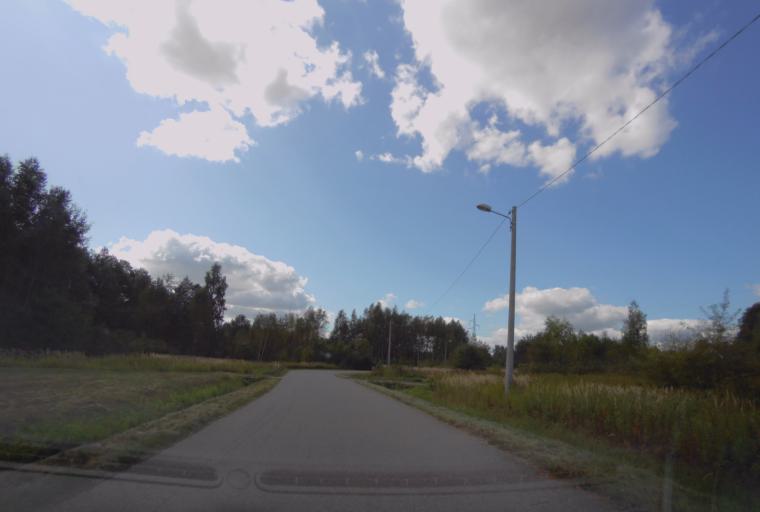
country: PL
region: Subcarpathian Voivodeship
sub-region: Powiat nizanski
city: Jezowe
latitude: 50.3915
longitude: 22.1191
